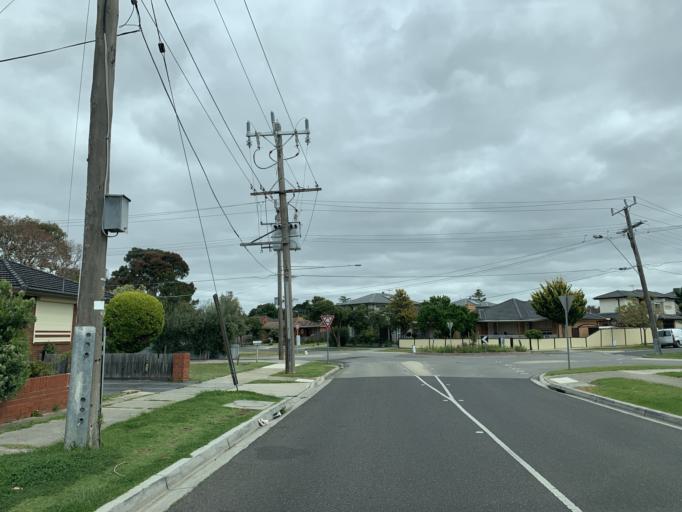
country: AU
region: Victoria
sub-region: Brimbank
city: Kealba
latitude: -37.7422
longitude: 144.8166
